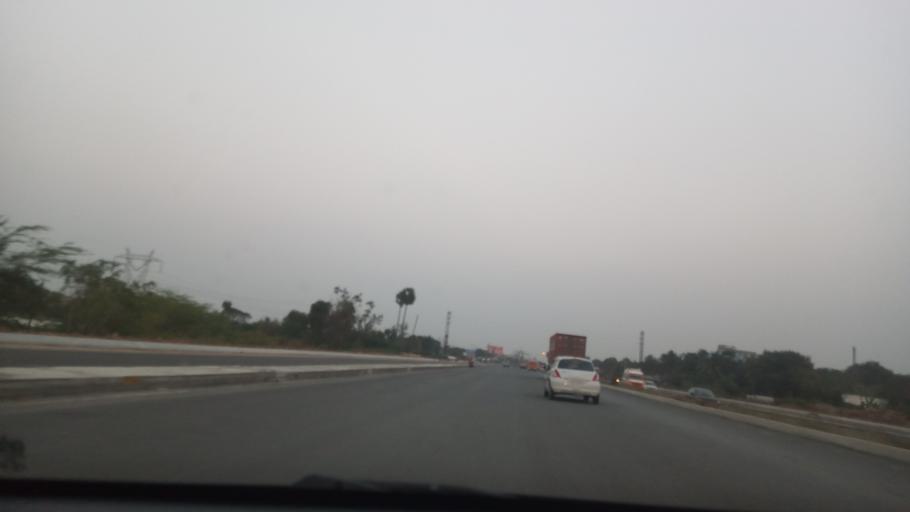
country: IN
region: Tamil Nadu
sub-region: Kancheepuram
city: Kanchipuram
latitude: 12.8745
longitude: 79.6780
